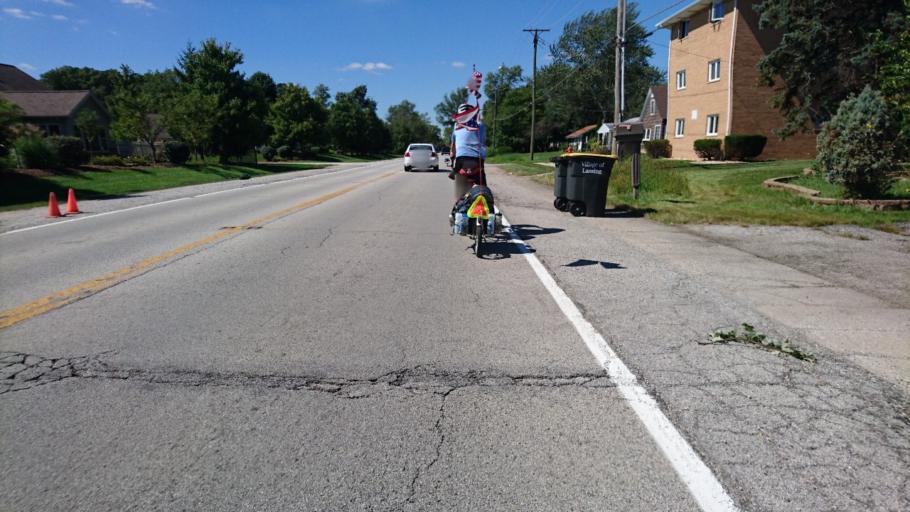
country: US
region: Illinois
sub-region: Cook County
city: Lansing
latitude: 41.5575
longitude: -87.5472
